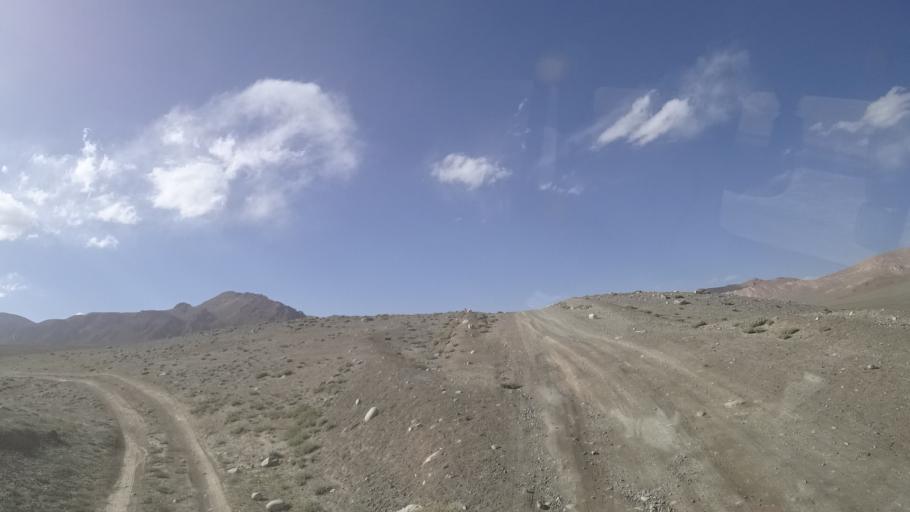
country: TJ
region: Gorno-Badakhshan
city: Murghob
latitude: 37.5771
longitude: 74.1568
